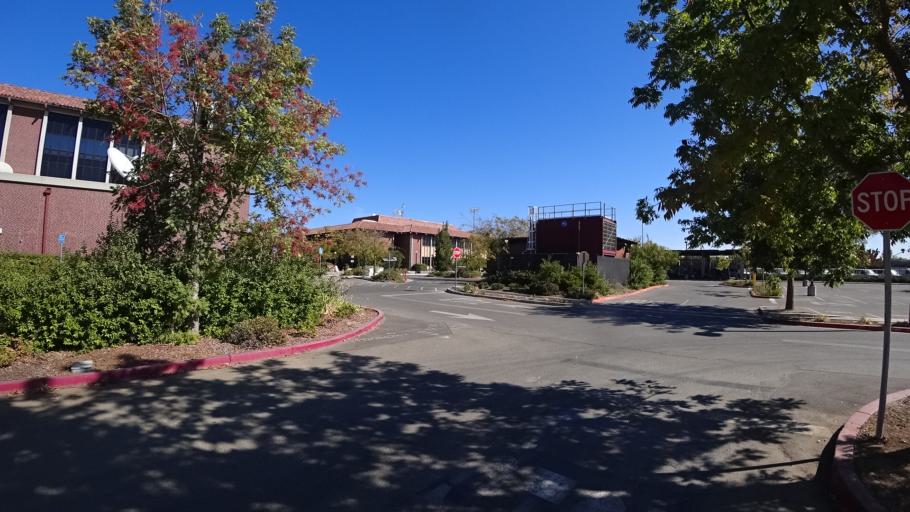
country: US
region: California
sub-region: Sacramento County
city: Sacramento
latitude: 38.5394
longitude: -121.4907
